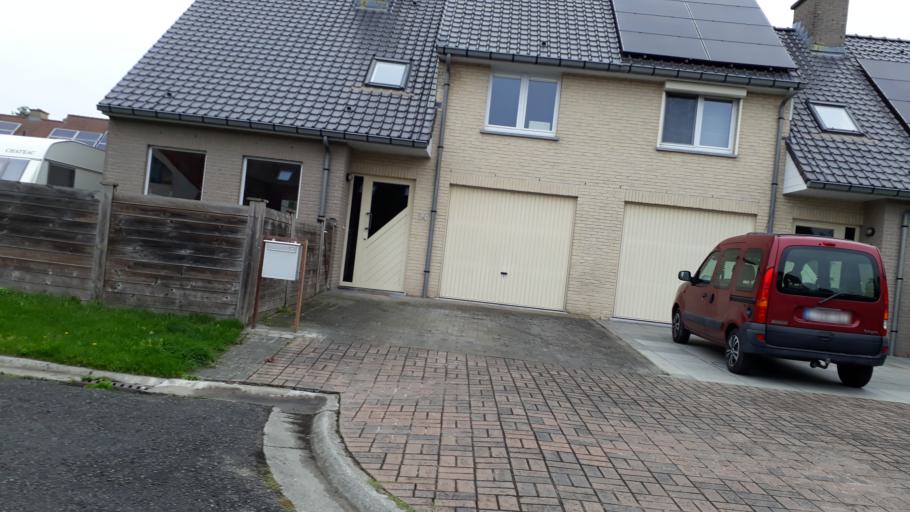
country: BE
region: Flanders
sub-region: Provincie West-Vlaanderen
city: Torhout
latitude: 51.0680
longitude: 3.1178
